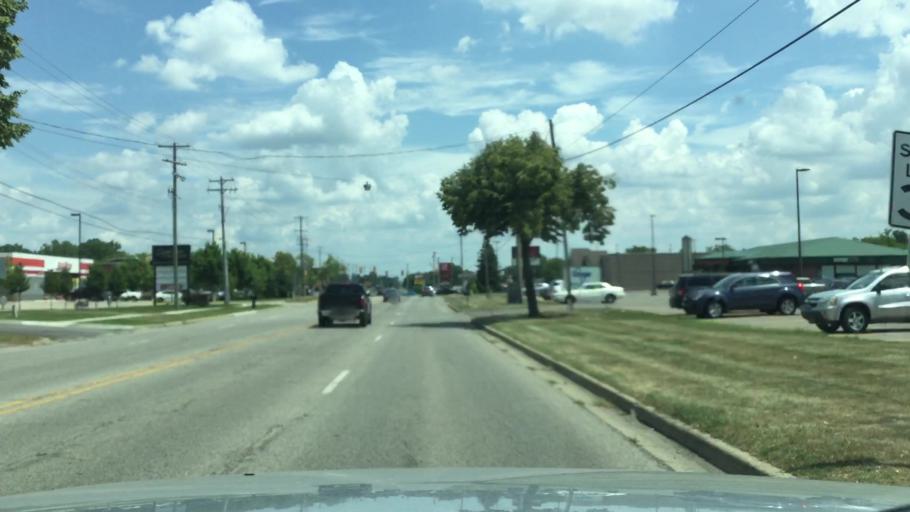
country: US
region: Michigan
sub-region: Genesee County
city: Flushing
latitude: 43.0600
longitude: -83.8163
